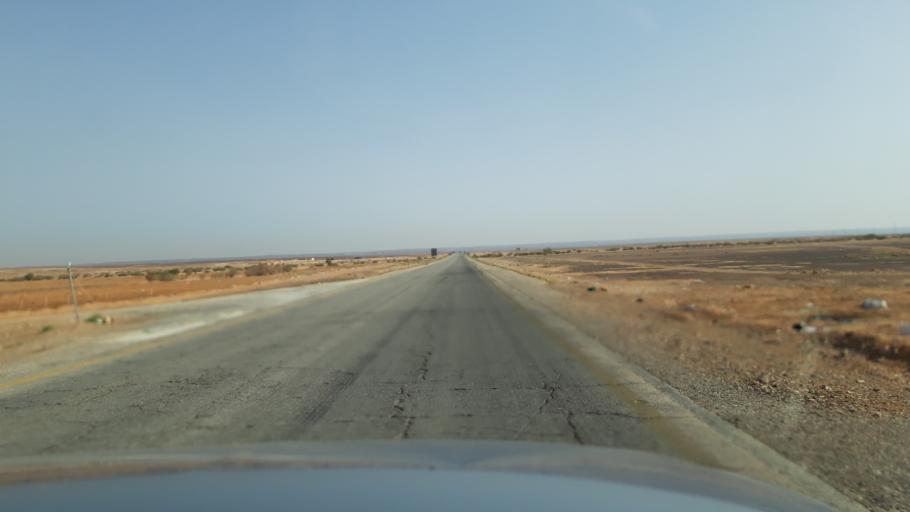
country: JO
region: Amman
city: Al Azraq ash Shamali
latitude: 31.7946
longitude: 36.5852
